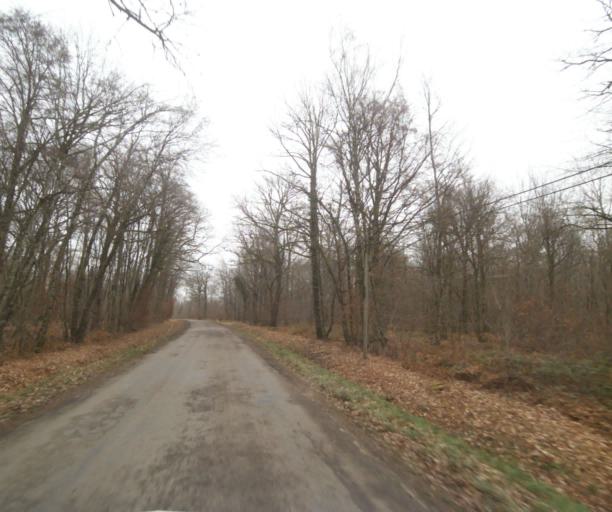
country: FR
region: Champagne-Ardenne
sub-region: Departement de la Haute-Marne
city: Wassy
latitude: 48.5287
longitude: 4.9780
